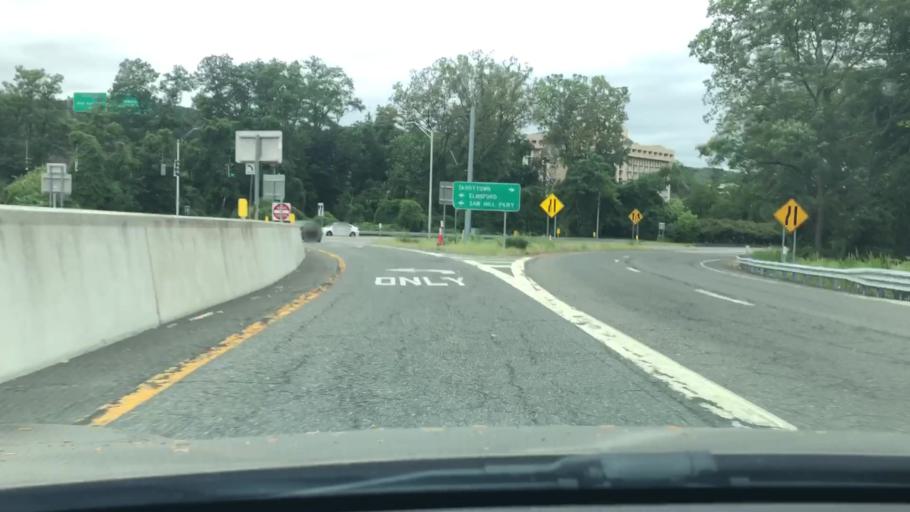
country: US
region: New York
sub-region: Westchester County
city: Elmsford
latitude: 41.0601
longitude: -73.8291
